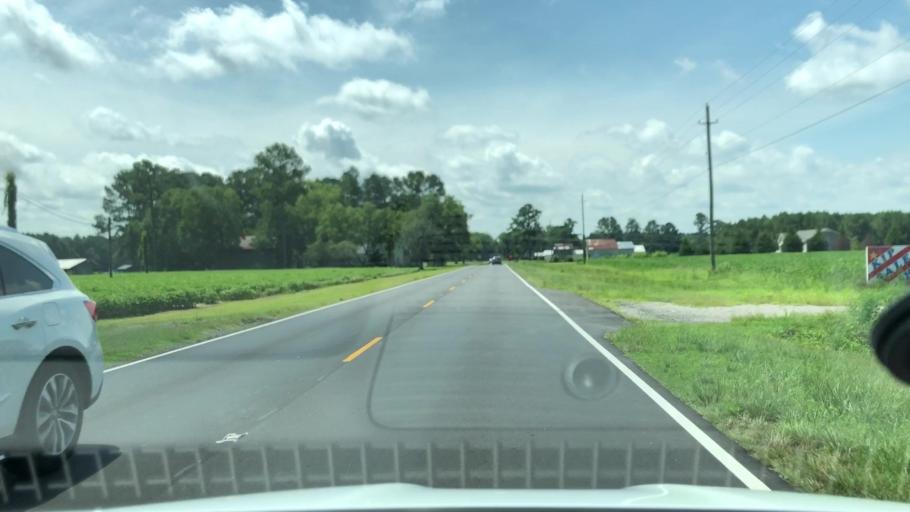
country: US
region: North Carolina
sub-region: Martin County
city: Williamston
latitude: 35.7454
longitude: -77.0759
